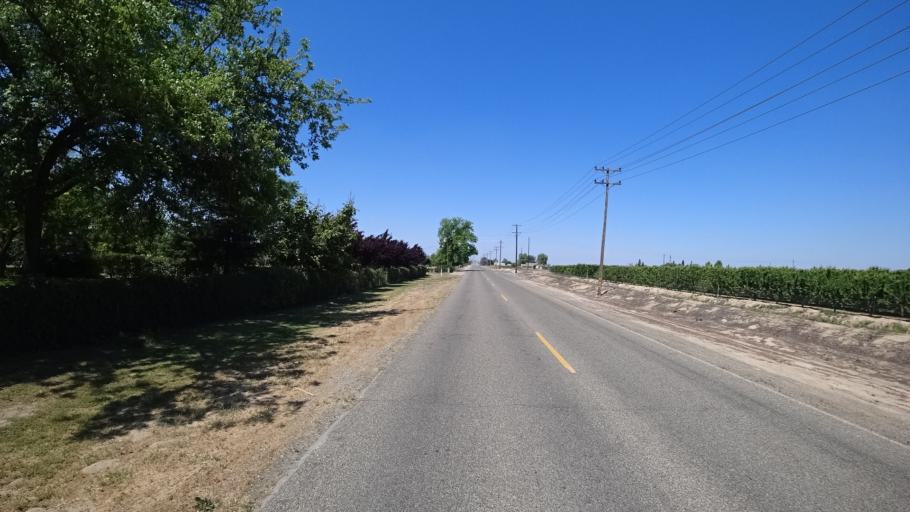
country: US
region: California
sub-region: Fresno County
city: Kingsburg
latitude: 36.4888
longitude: -119.5733
